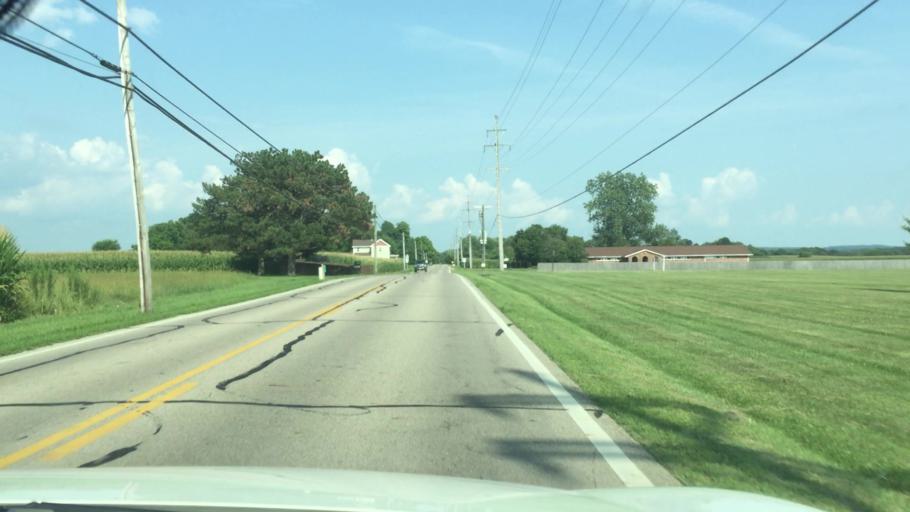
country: US
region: Ohio
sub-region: Clark County
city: Northridge
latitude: 39.9942
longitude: -83.7514
